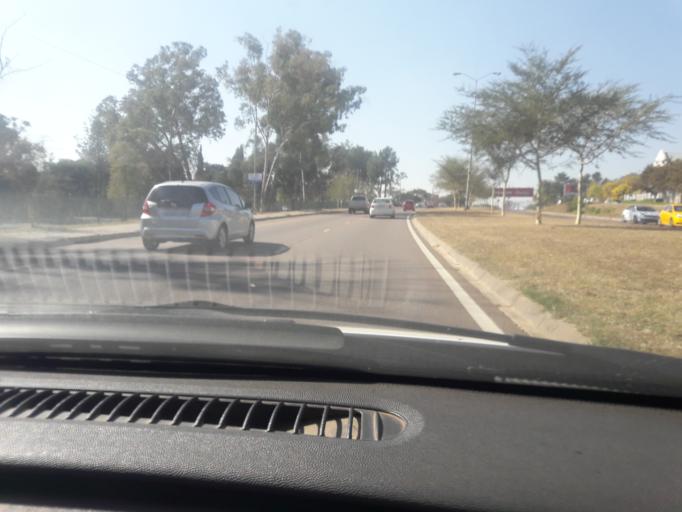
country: ZA
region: Gauteng
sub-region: City of Tshwane Metropolitan Municipality
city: Pretoria
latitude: -25.7655
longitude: 28.3120
